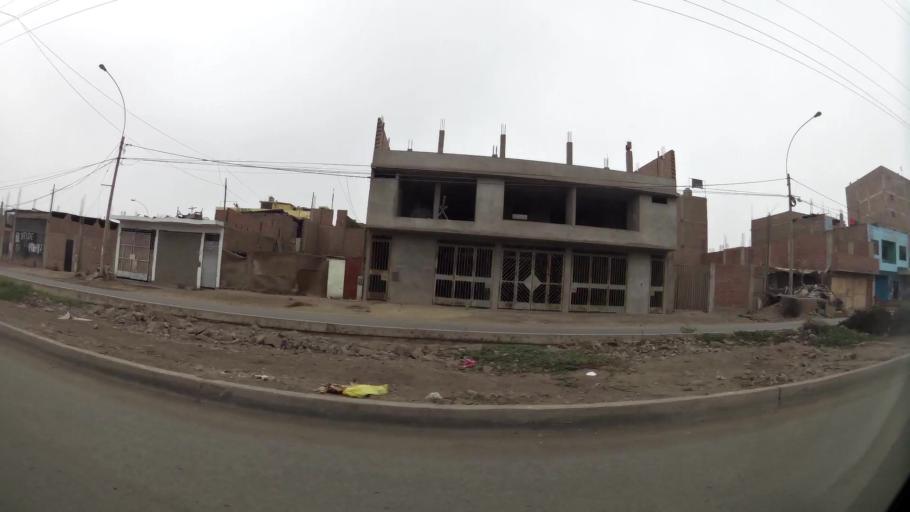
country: PE
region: Lima
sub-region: Lima
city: Urb. Santo Domingo
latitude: -11.8850
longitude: -77.0396
